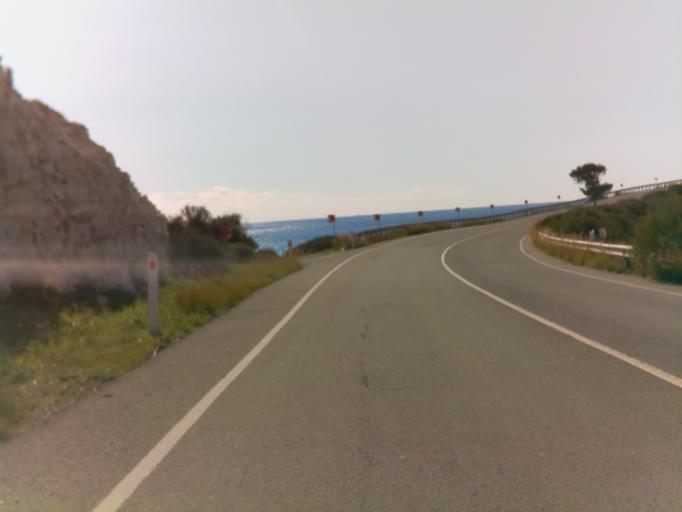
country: CY
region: Limassol
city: Pissouri
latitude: 34.6595
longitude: 32.6511
